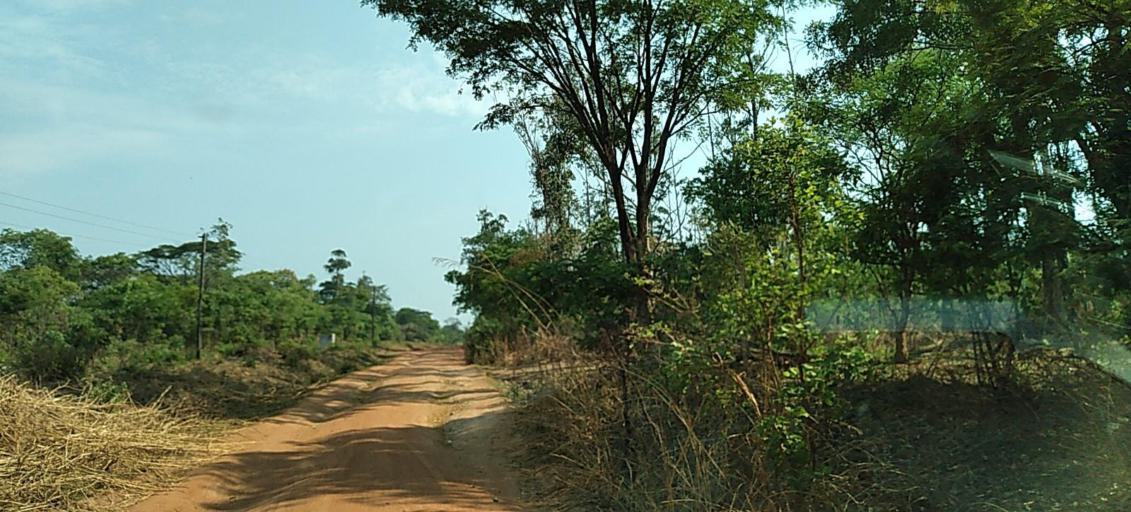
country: ZM
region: Copperbelt
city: Kalulushi
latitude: -13.0053
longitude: 27.8132
